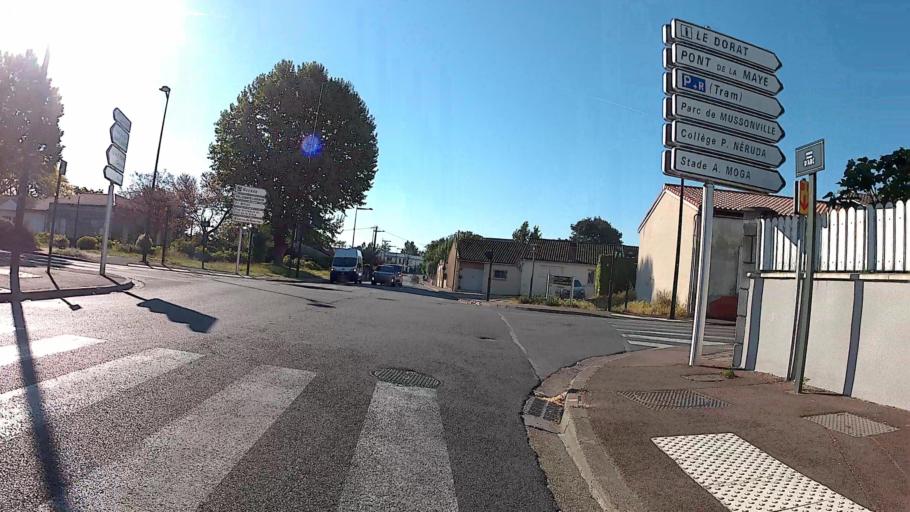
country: FR
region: Aquitaine
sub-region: Departement de la Gironde
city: Begles
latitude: 44.8004
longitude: -0.5433
